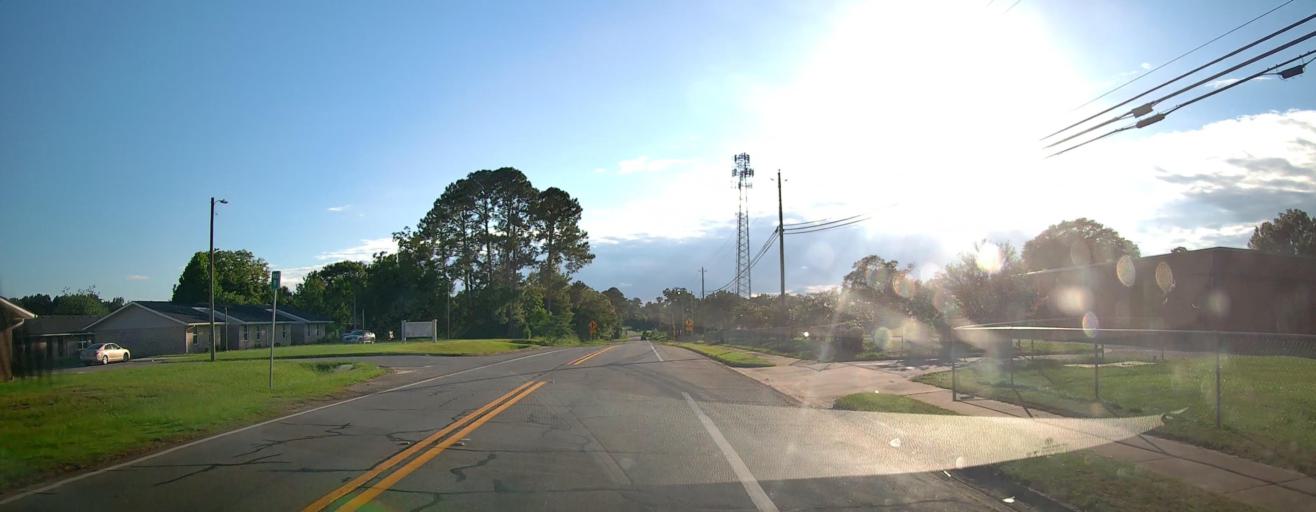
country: US
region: Georgia
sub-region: Pulaski County
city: Hawkinsville
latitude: 32.2794
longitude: -83.4901
